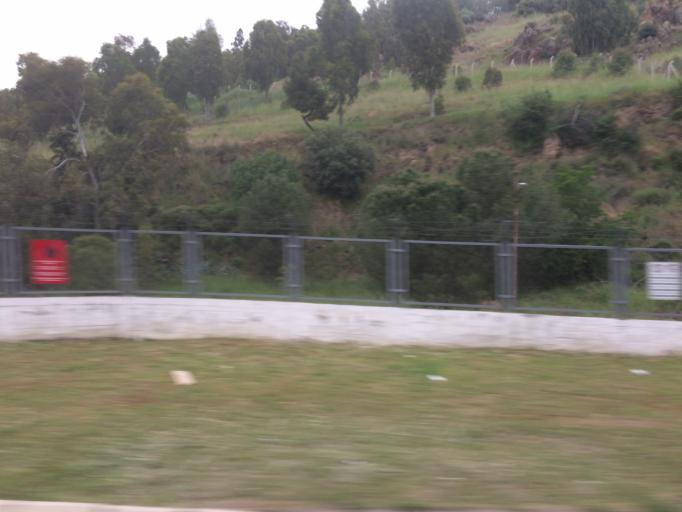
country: TR
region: Izmir
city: Karsiyaka
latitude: 38.4685
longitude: 27.1531
